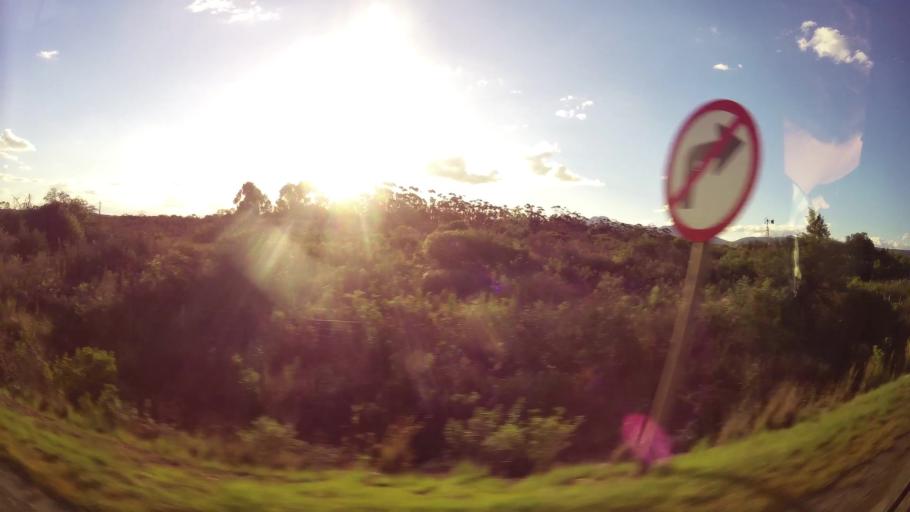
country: ZA
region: Western Cape
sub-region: Eden District Municipality
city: Riversdale
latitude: -34.0905
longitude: 20.9775
